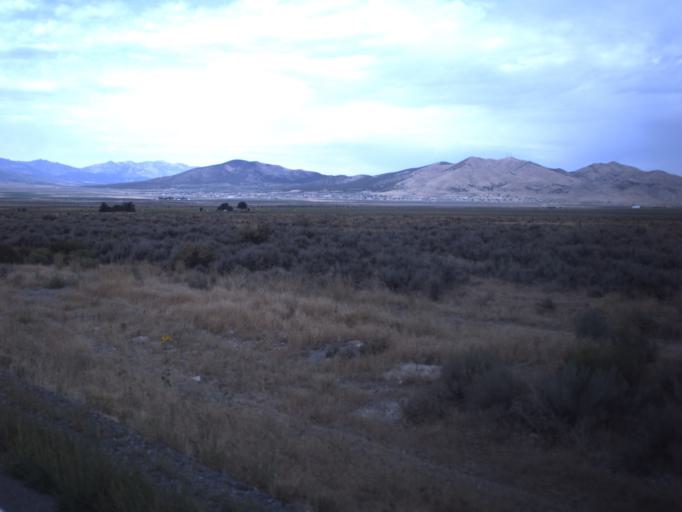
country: US
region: Utah
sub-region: Tooele County
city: Tooele
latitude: 40.3775
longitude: -112.3768
